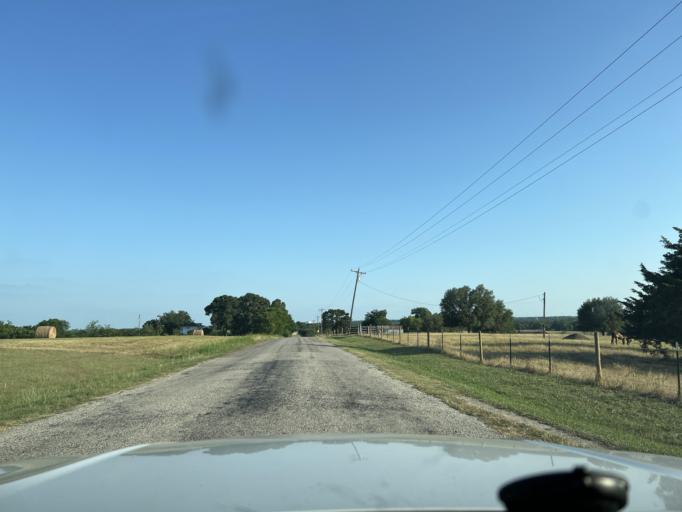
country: US
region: Texas
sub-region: Washington County
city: Brenham
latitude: 30.2266
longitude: -96.3797
